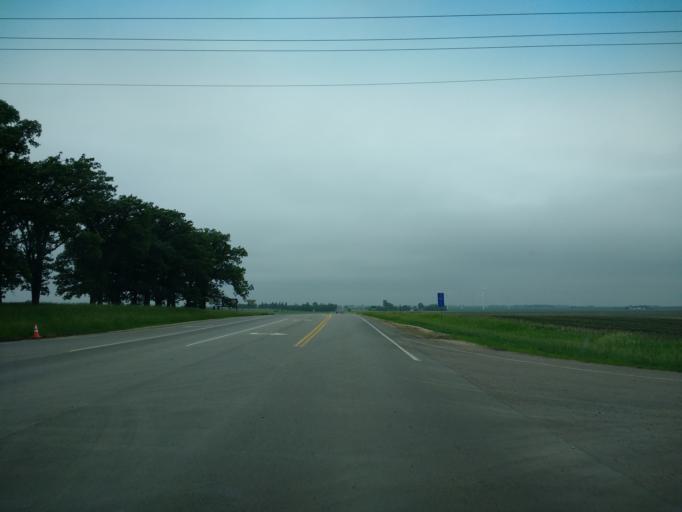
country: US
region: Iowa
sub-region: O'Brien County
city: Sanborn
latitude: 43.1861
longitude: -95.6636
